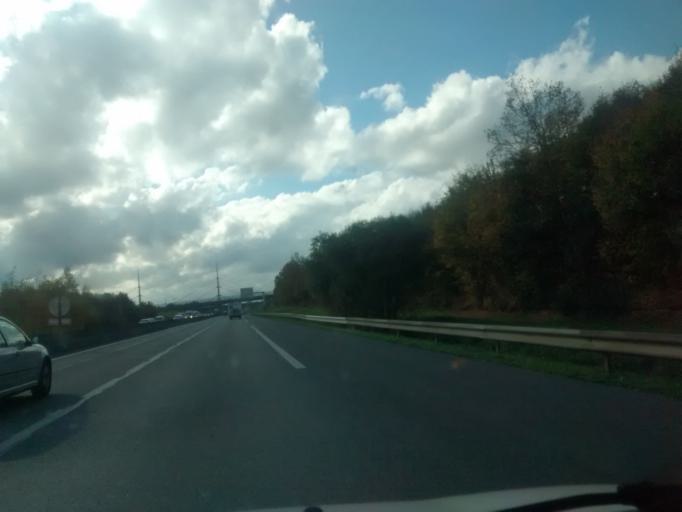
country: FR
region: Brittany
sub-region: Departement d'Ille-et-Vilaine
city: Chantepie
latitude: 48.0868
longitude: -1.6371
